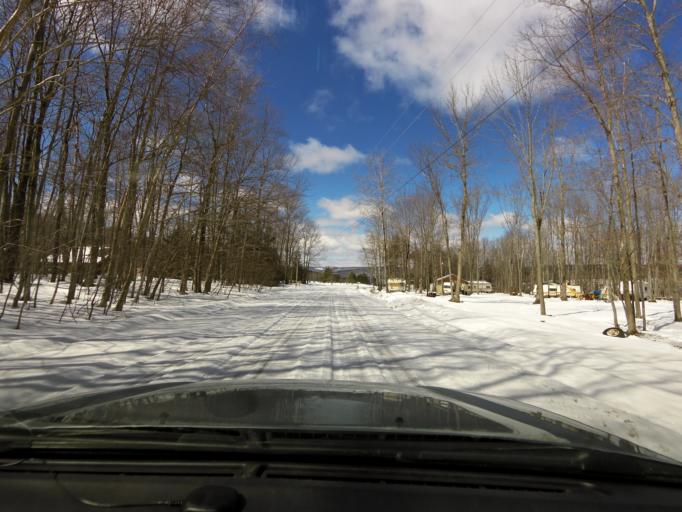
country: US
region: New York
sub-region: Cattaraugus County
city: Franklinville
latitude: 42.3428
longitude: -78.4079
